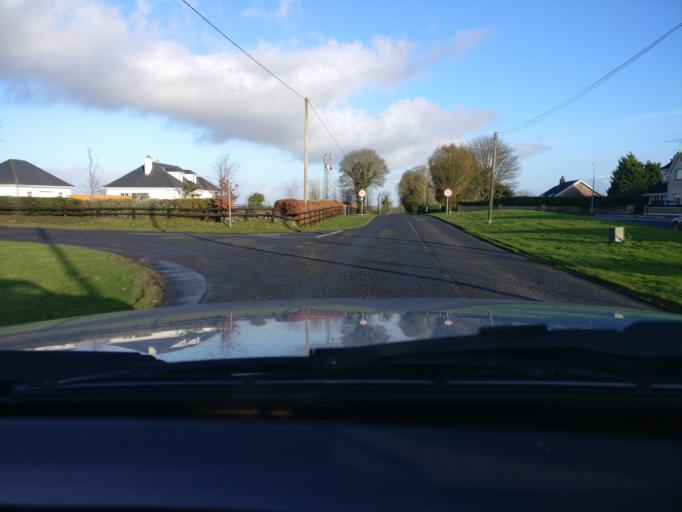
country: IE
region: Ulster
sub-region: An Cabhan
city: Mullagh
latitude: 53.7153
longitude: -7.0178
